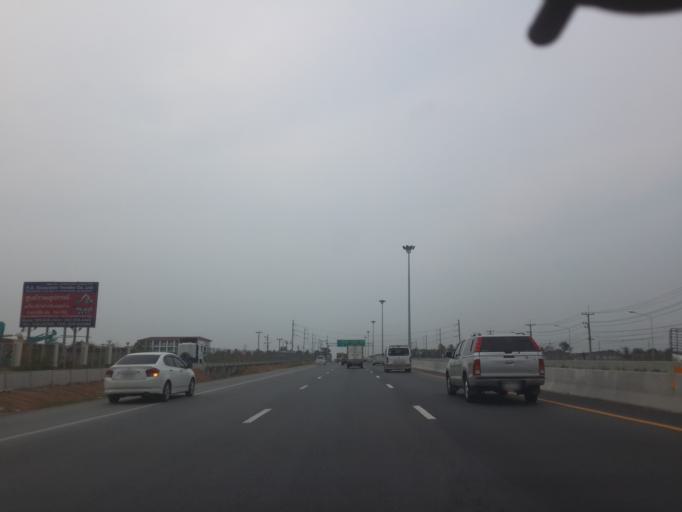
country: TH
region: Chon Buri
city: Ban Talat Bueng
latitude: 13.0905
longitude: 100.9906
